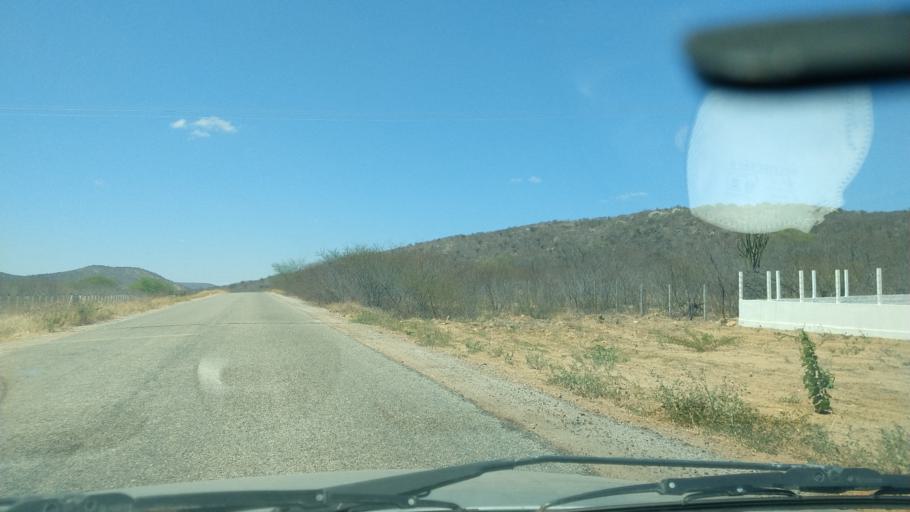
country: BR
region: Rio Grande do Norte
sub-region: Sao Tome
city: Sao Tome
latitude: -5.9739
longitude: -36.1383
